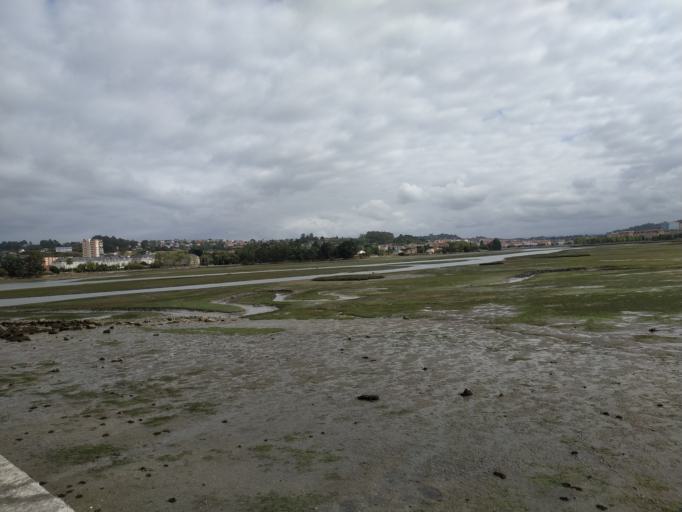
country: ES
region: Galicia
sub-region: Provincia da Coruna
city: Culleredo
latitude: 43.3254
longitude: -8.3818
